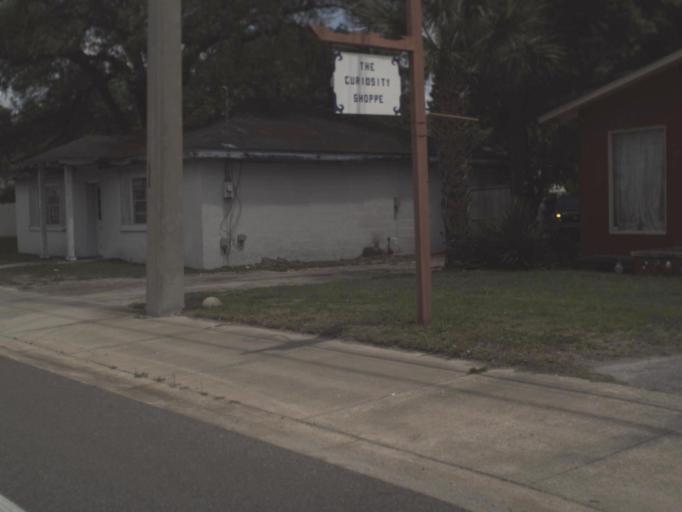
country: US
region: Florida
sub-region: Saint Johns County
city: Fruit Cove
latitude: 30.1429
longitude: -81.5175
